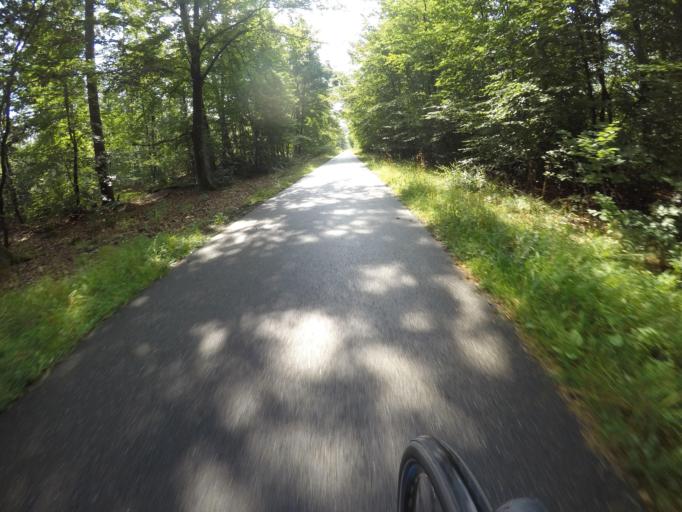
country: DE
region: Baden-Wuerttemberg
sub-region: Karlsruhe Region
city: Hockenheim
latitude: 49.3291
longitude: 8.5874
